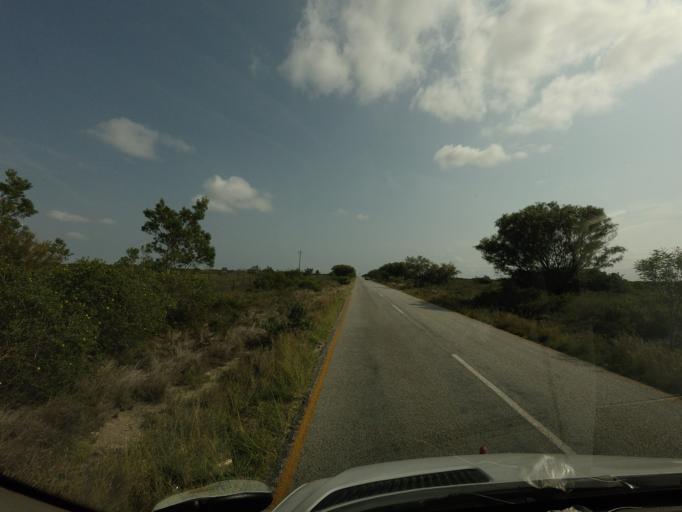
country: ZA
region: Eastern Cape
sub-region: Nelson Mandela Bay Metropolitan Municipality
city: Uitenhage
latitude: -33.6969
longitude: 25.5886
